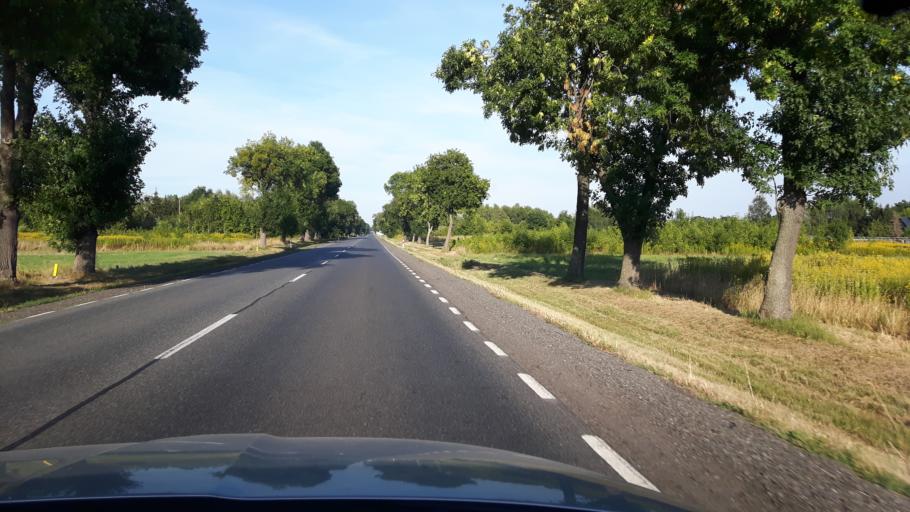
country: PL
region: Masovian Voivodeship
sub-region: Powiat nowodworski
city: Brody-Parcele
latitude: 52.4862
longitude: 20.8030
